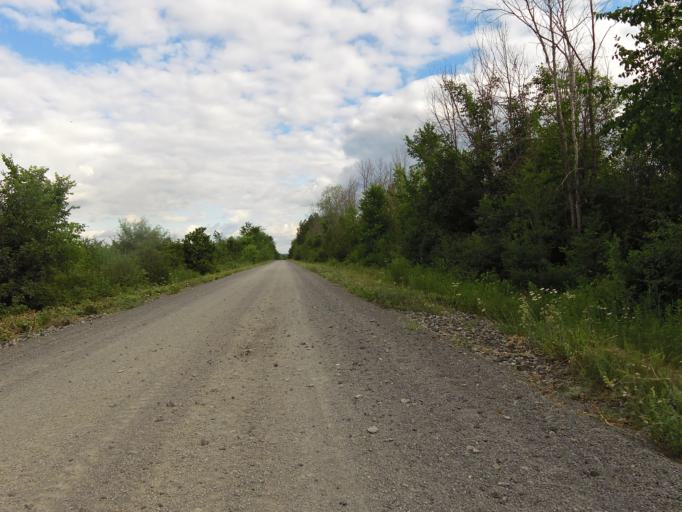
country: CA
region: Ontario
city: Arnprior
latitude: 45.2914
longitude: -76.2561
